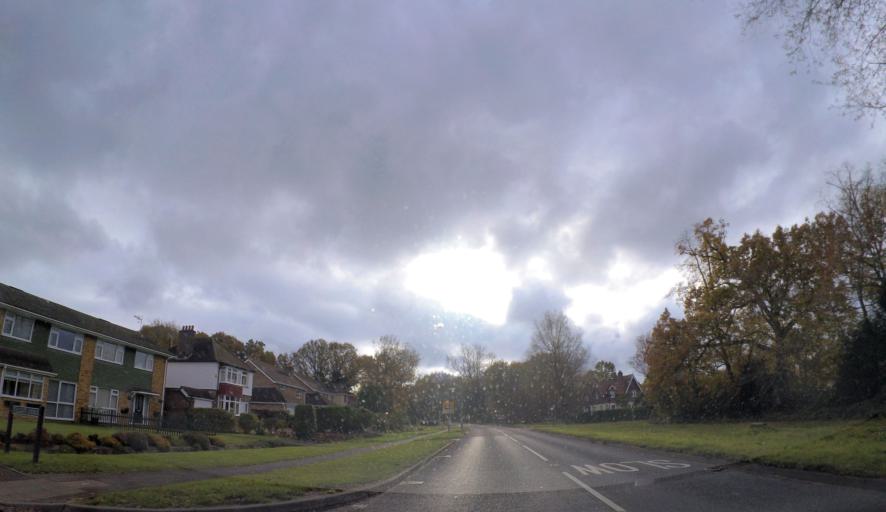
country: GB
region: England
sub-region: Surrey
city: Salfords
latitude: 51.2139
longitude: -0.1753
